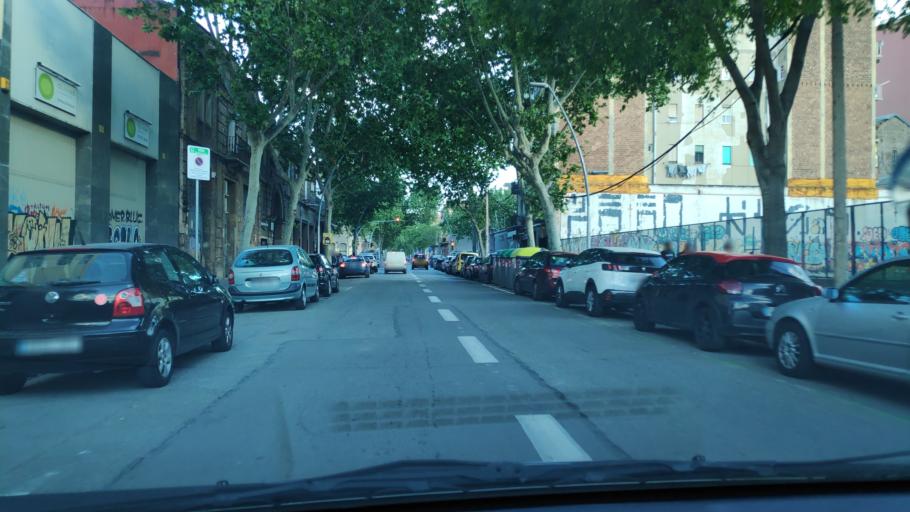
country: ES
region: Catalonia
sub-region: Provincia de Barcelona
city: Sant Marti
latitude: 41.3972
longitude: 2.1906
